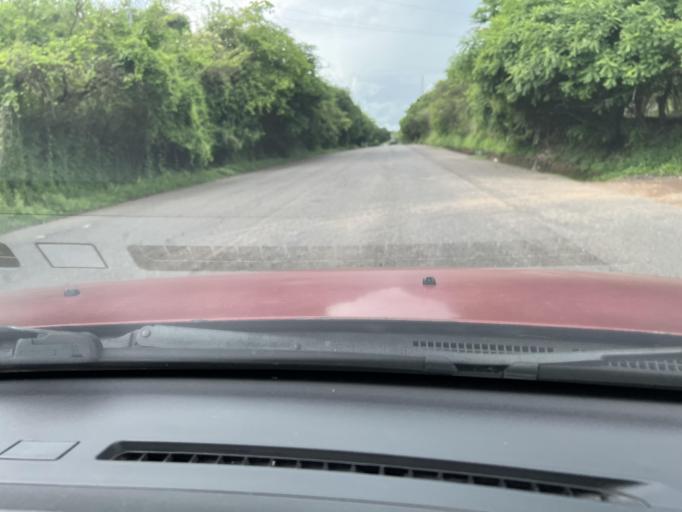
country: SV
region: La Union
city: San Alejo
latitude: 13.3962
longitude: -87.8997
